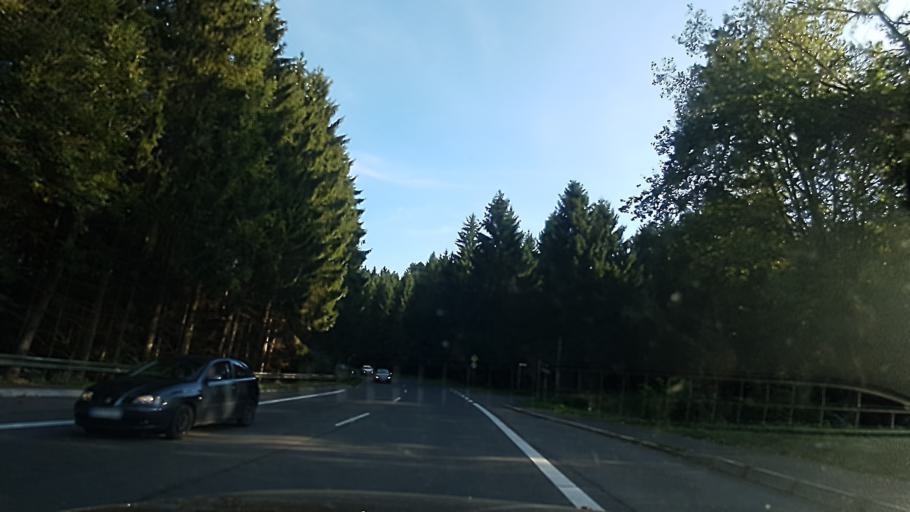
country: DE
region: North Rhine-Westphalia
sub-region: Regierungsbezirk Koln
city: Marienheide
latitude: 51.1054
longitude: 7.4896
